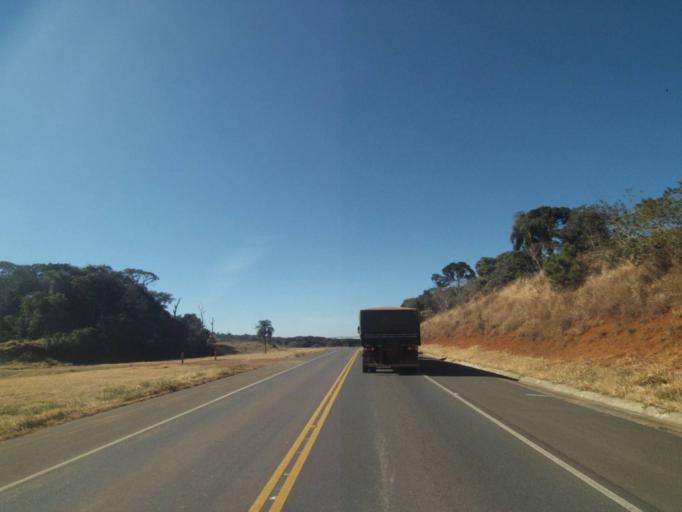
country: BR
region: Parana
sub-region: Tibagi
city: Tibagi
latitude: -24.5799
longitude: -50.4449
